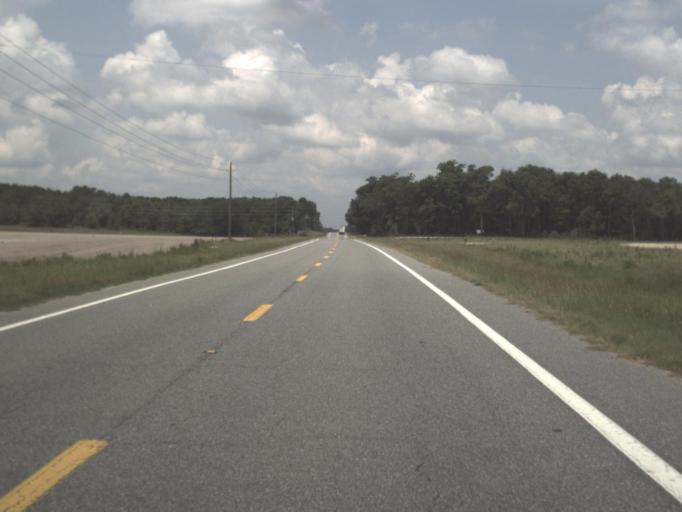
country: US
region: Florida
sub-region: Hamilton County
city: Jasper
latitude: 30.4897
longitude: -83.1624
